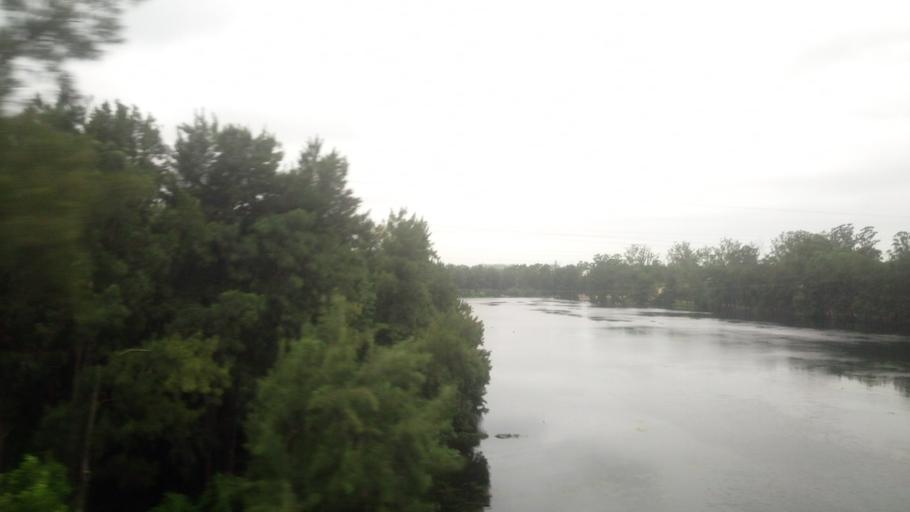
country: AU
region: New South Wales
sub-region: Penrith Municipality
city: Penrith
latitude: -33.7455
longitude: 150.6812
